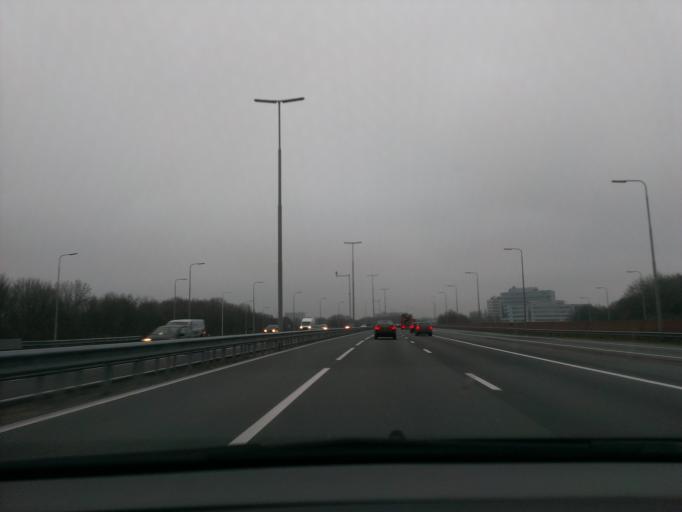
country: NL
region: Overijssel
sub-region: Gemeente Zwolle
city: Zwolle
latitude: 52.5142
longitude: 6.0787
